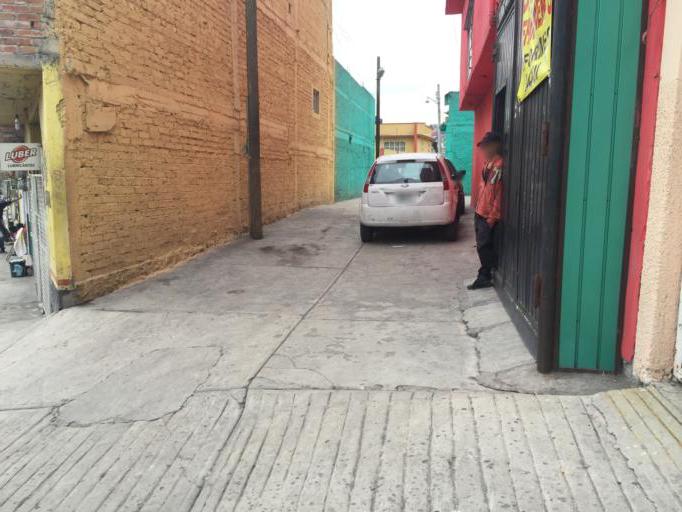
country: MX
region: Mexico
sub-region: Tlalnepantla de Baz
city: Puerto Escondido (Tepeolulco Puerto Escondido)
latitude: 19.5591
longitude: -99.0826
